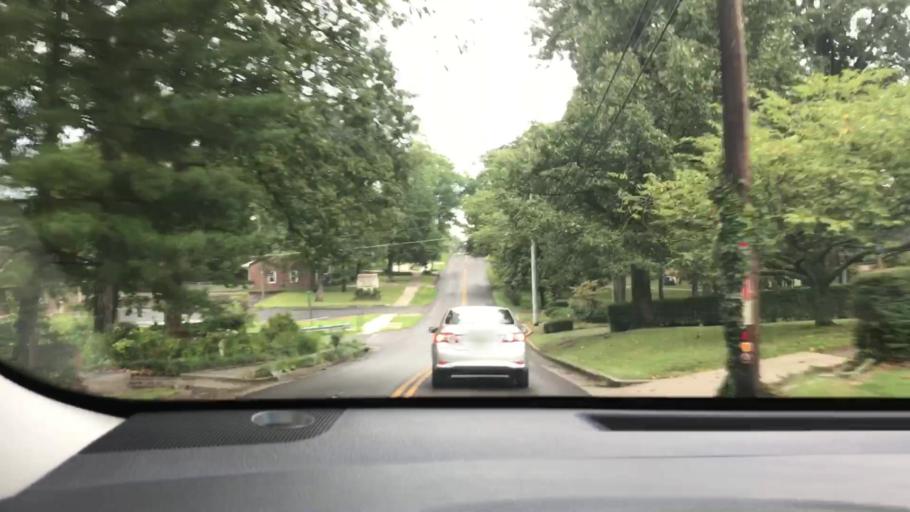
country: US
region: Kentucky
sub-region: Calloway County
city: Murray
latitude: 36.6030
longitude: -88.3224
